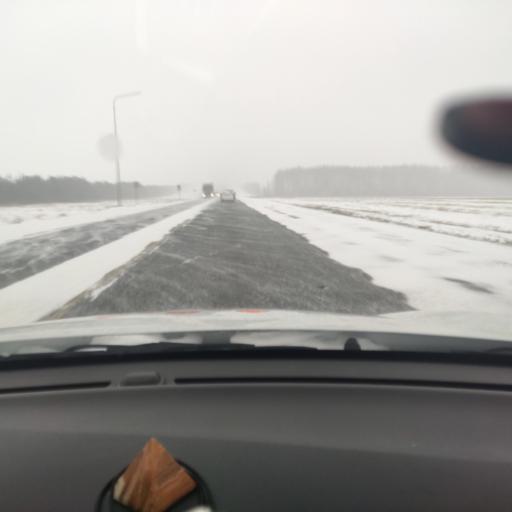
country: RU
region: Tatarstan
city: Verkhniy Uslon
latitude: 55.6619
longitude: 48.8593
